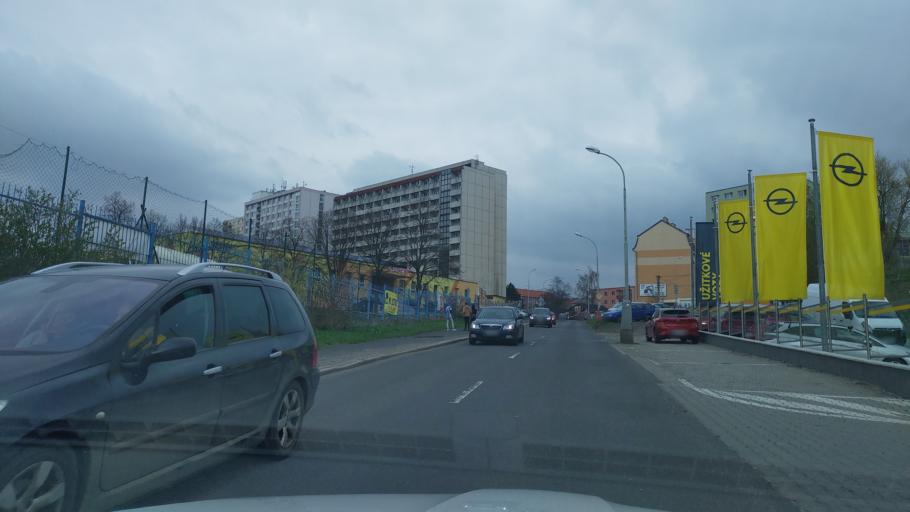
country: CZ
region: Ustecky
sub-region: Okres Usti nad Labem
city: Usti nad Labem
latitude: 50.6641
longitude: 14.0120
